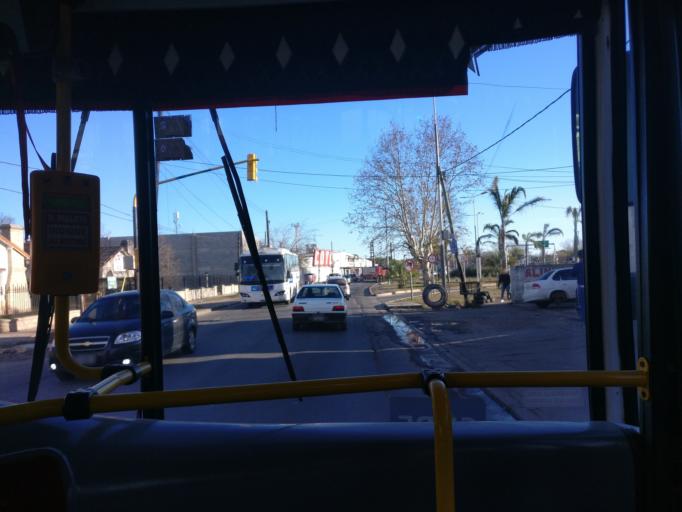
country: AR
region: Buenos Aires
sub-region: Partido de Ezeiza
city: Ezeiza
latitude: -34.8923
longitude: -58.5709
